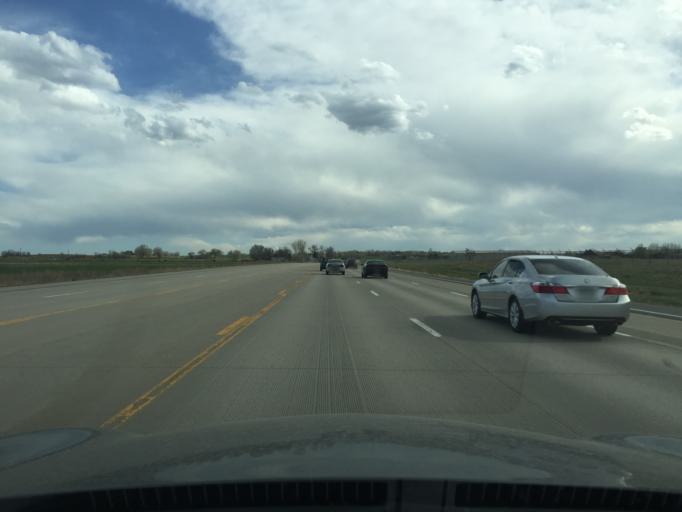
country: US
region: Colorado
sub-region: Boulder County
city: Lafayette
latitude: 40.0435
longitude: -105.1027
